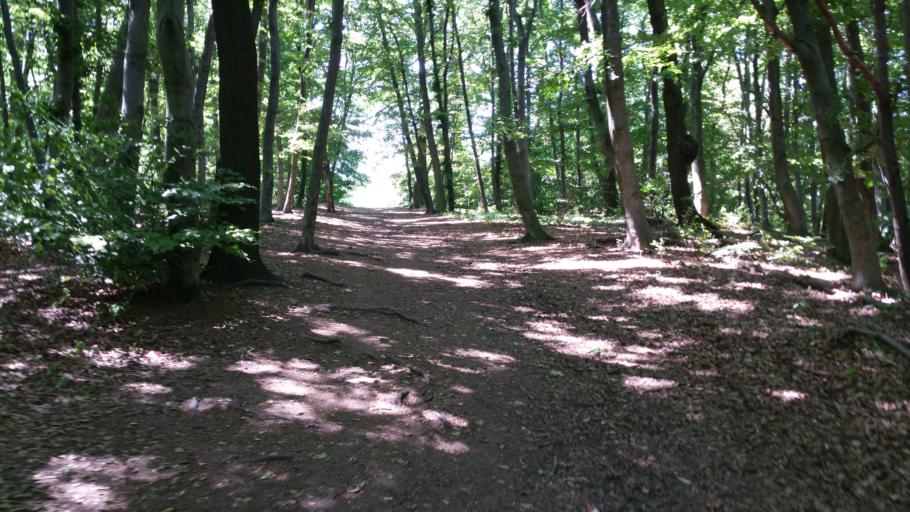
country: AT
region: Lower Austria
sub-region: Politischer Bezirk Wien-Umgebung
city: Purkersdorf
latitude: 48.2223
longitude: 16.2679
